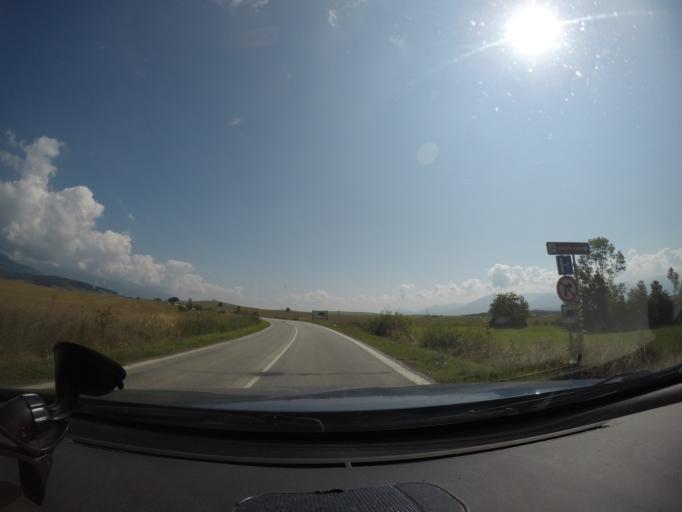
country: SK
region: Zilinsky
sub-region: Okres Liptovsky Mikulas
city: Liptovsky Mikulas
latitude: 49.1314
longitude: 19.5184
